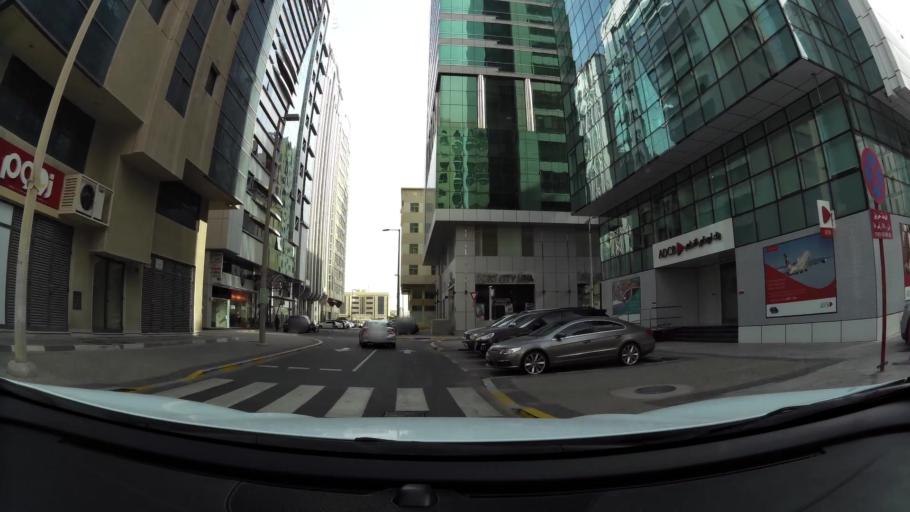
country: AE
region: Abu Dhabi
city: Abu Dhabi
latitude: 24.4669
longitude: 54.3841
